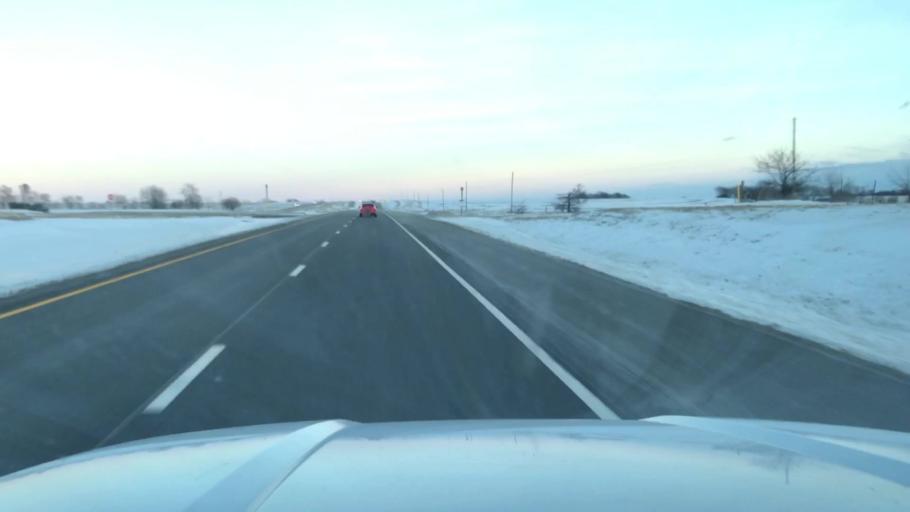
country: US
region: Missouri
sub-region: DeKalb County
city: Maysville
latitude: 39.7615
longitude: -94.3761
